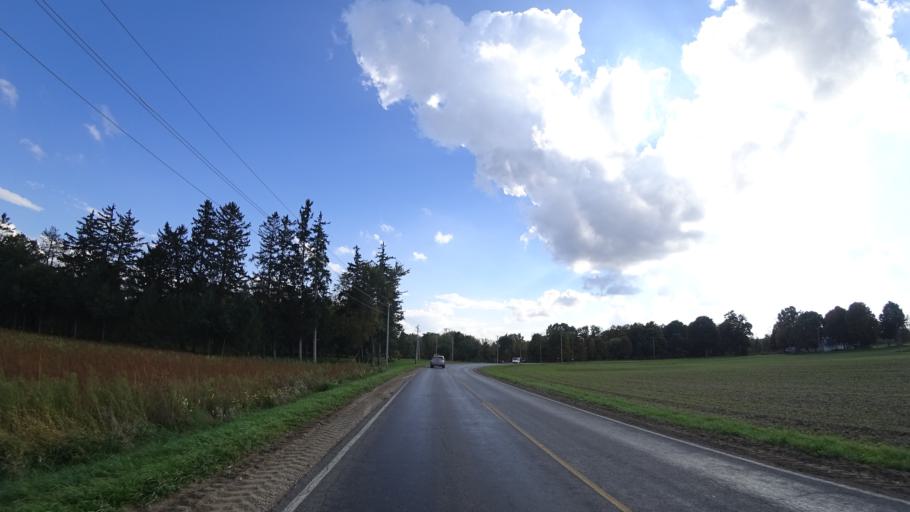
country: US
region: Michigan
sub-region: Saint Joseph County
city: Centreville
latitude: 41.9346
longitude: -85.5277
